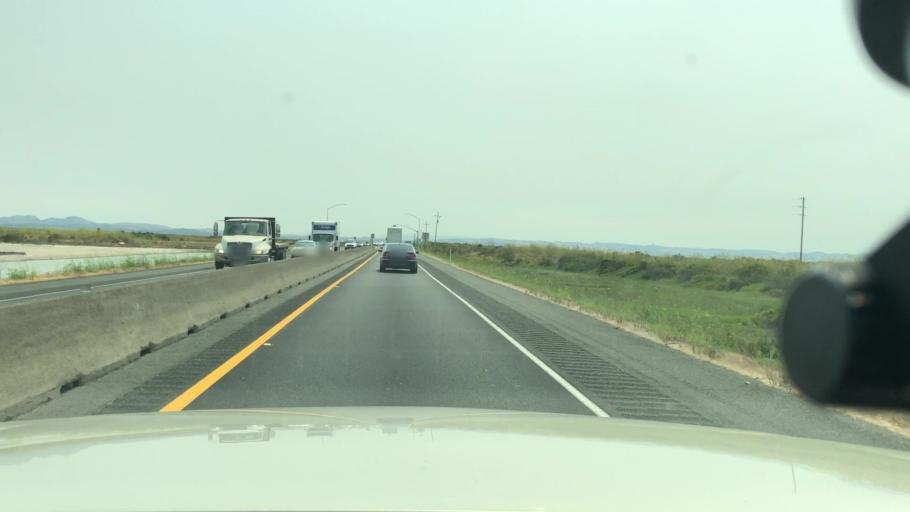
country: US
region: California
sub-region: Napa County
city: American Canyon
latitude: 38.1498
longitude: -122.3829
